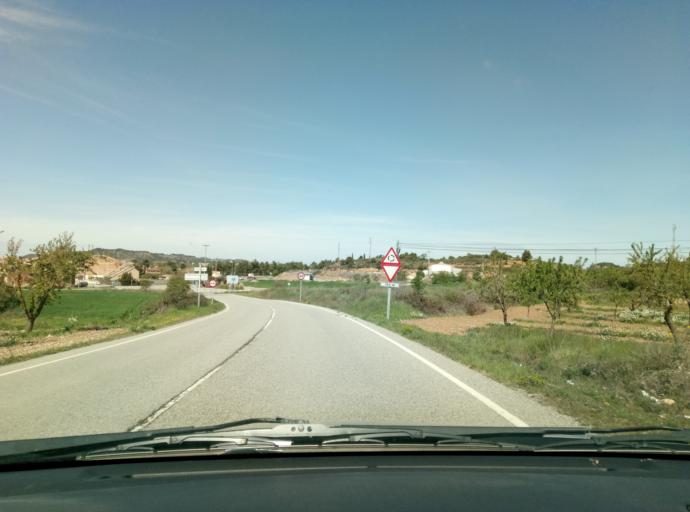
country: ES
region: Catalonia
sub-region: Provincia de Lleida
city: Vinaixa
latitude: 41.4233
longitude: 0.9464
